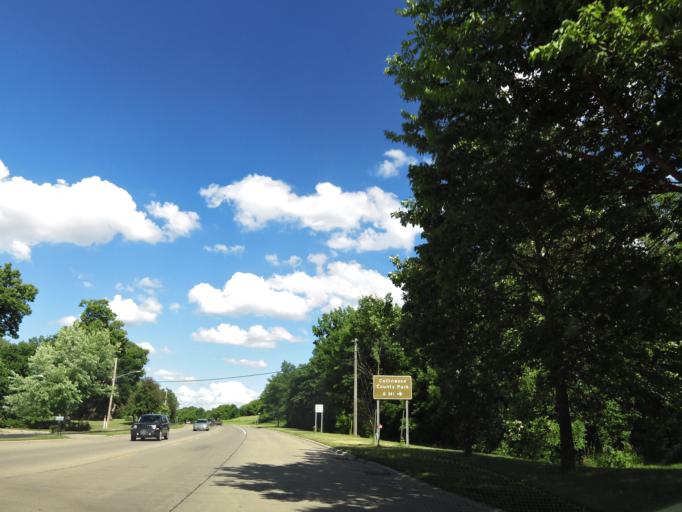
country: US
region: Minnesota
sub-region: Meeker County
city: Dassel
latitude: 45.0811
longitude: -94.2989
